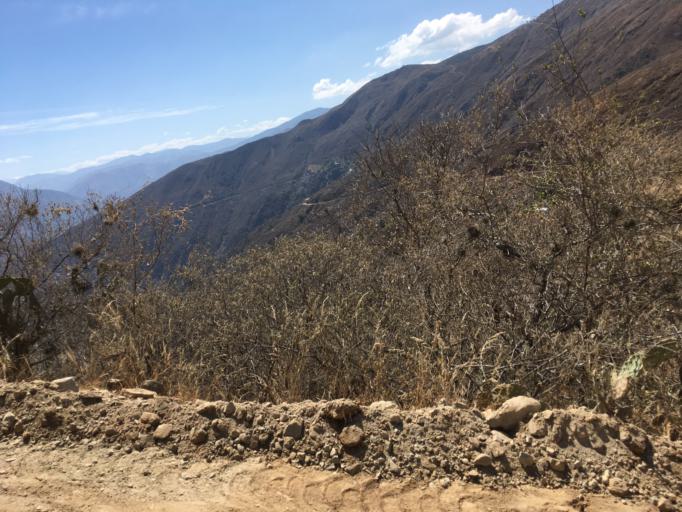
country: CO
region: Santander
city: Aratoca
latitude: 6.7931
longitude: -72.9949
